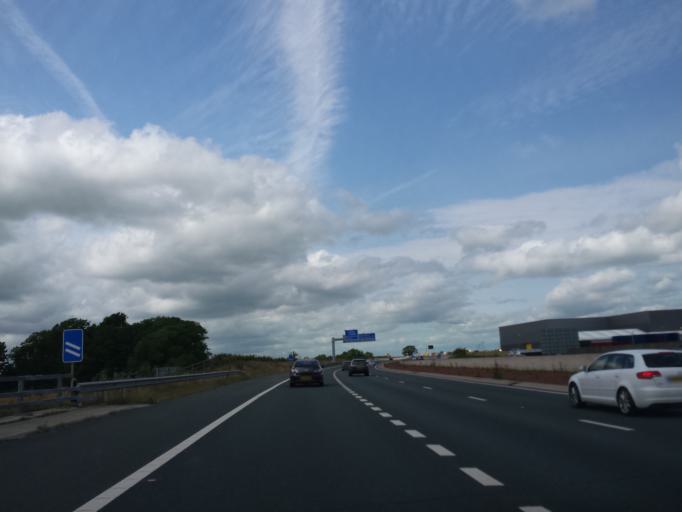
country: GB
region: England
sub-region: North Yorkshire
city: Bedale
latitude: 54.3015
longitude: -1.5679
